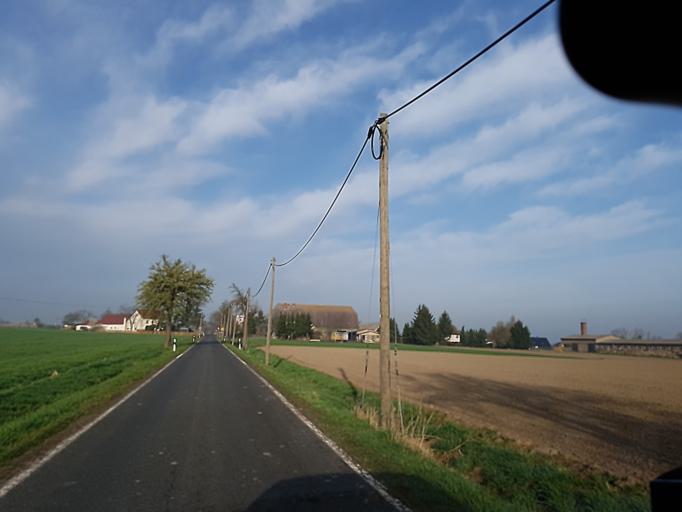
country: DE
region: Saxony
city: Stauchitz
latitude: 51.2613
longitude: 13.1713
